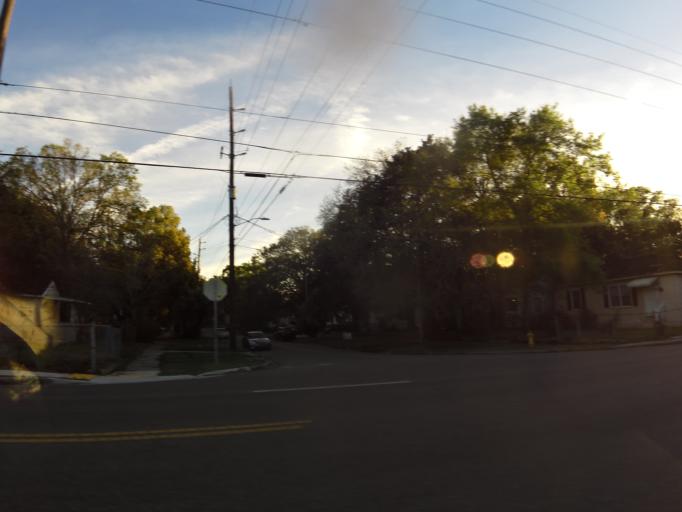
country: US
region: Florida
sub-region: Duval County
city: Jacksonville
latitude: 30.3366
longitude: -81.7130
